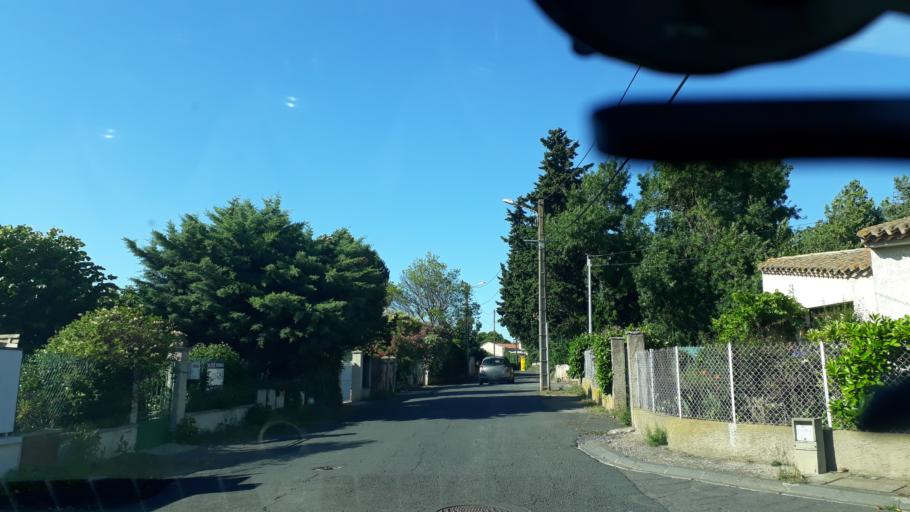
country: FR
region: Languedoc-Roussillon
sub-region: Departement de l'Herault
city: Agde
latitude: 43.3160
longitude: 3.4774
